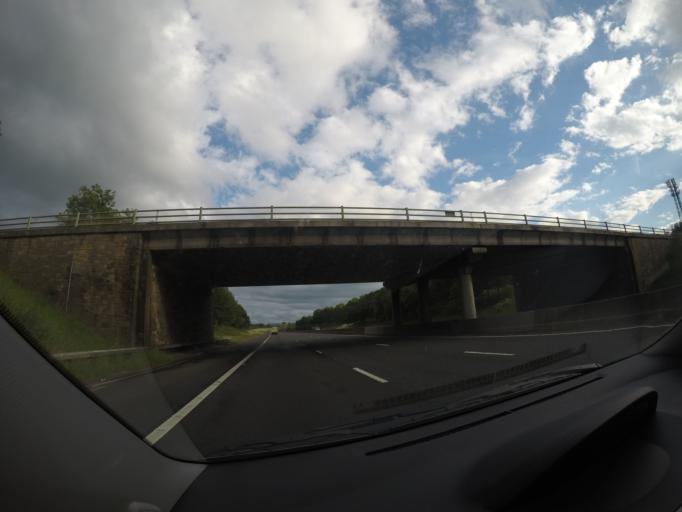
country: GB
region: England
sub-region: Cumbria
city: Penrith
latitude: 54.6932
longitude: -2.7915
